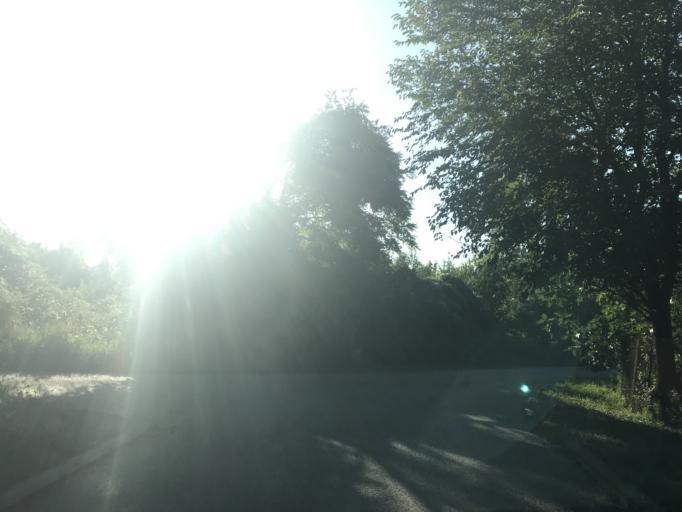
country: RS
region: Autonomna Pokrajina Vojvodina
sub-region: Juznobacki Okrug
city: Novi Sad
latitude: 45.2129
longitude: 19.7996
